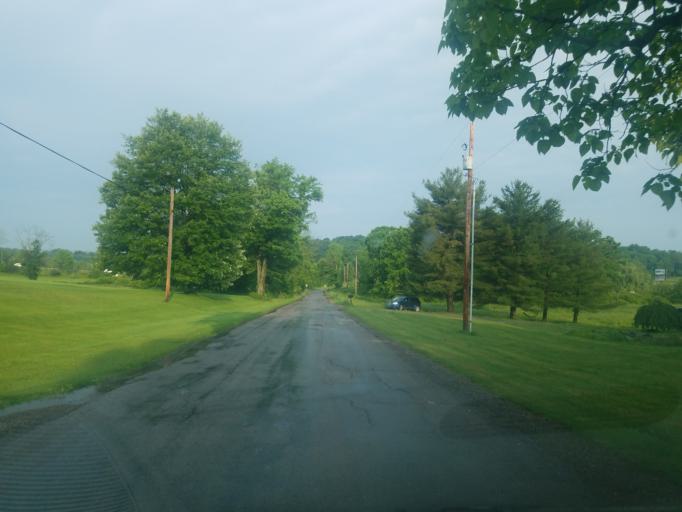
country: US
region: Ohio
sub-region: Carroll County
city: Carrollton
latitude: 40.6337
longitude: -81.1088
